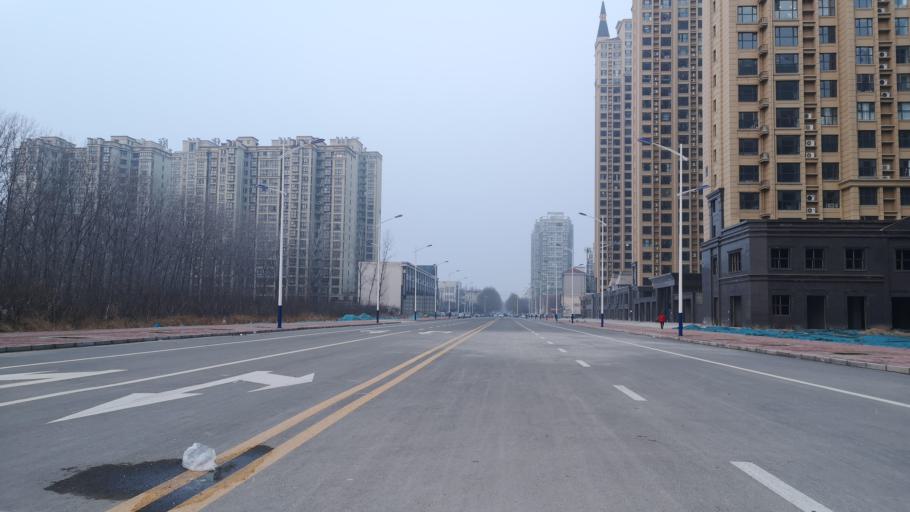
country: CN
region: Henan Sheng
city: Zhongyuanlu
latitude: 35.7502
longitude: 115.0600
